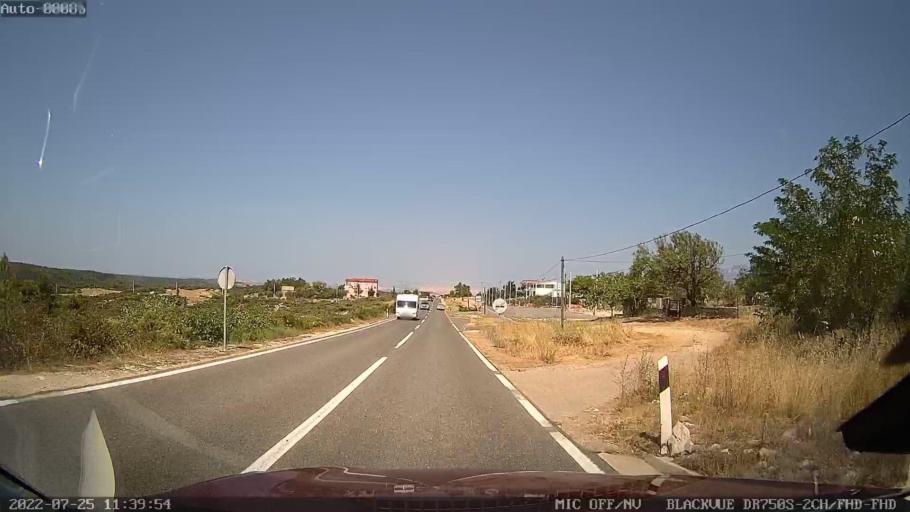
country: HR
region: Zadarska
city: Razanac
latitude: 44.2595
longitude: 15.3668
